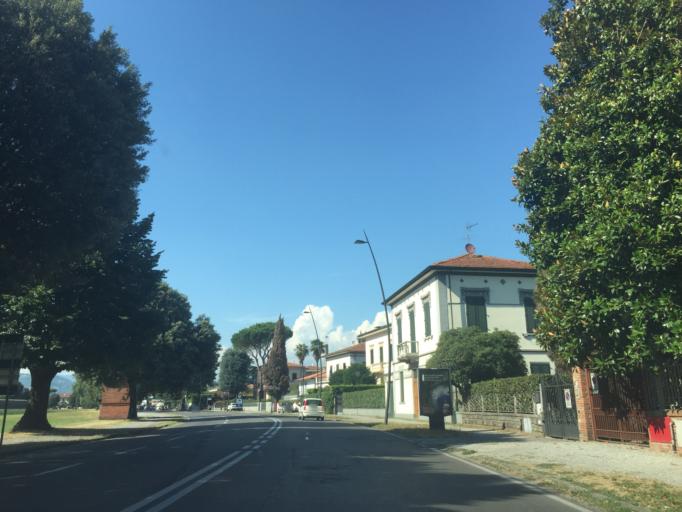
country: IT
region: Tuscany
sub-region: Provincia di Lucca
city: Lucca
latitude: 43.8446
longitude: 10.5163
